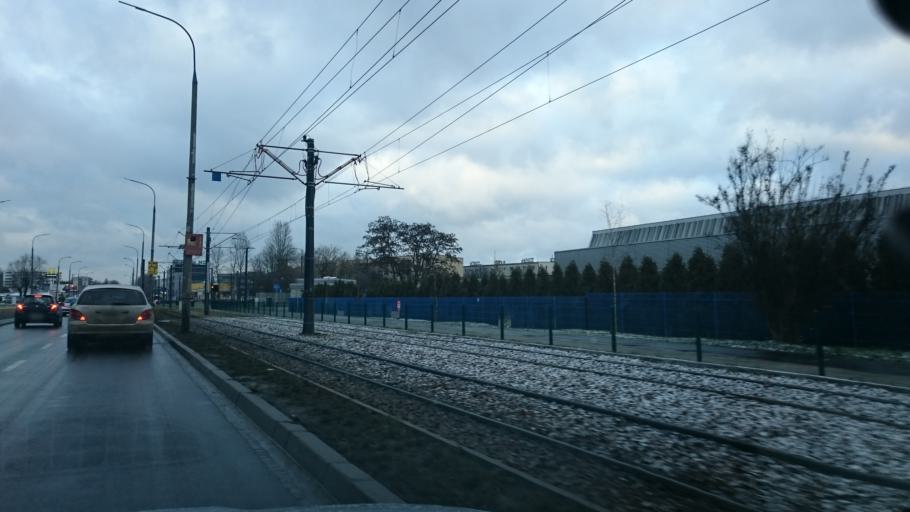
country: PL
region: Lesser Poland Voivodeship
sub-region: Krakow
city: Krakow
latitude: 50.0300
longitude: 19.9736
